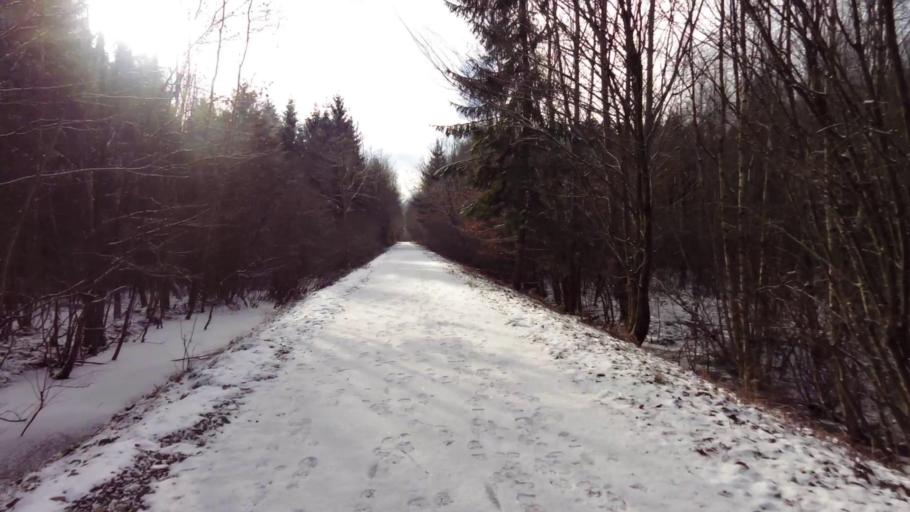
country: PL
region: West Pomeranian Voivodeship
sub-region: Powiat swidwinski
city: Polczyn-Zdroj
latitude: 53.7433
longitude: 16.0571
